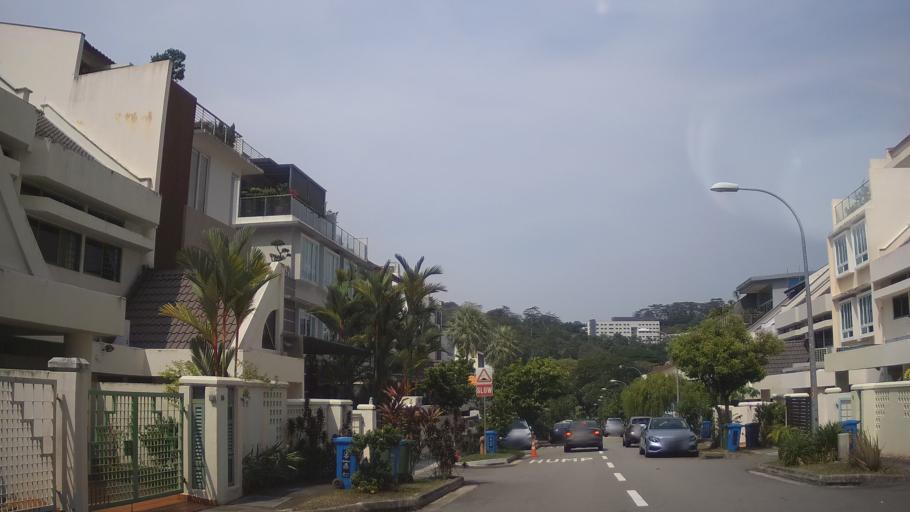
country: MY
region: Johor
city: Johor Bahru
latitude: 1.3723
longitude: 103.7659
